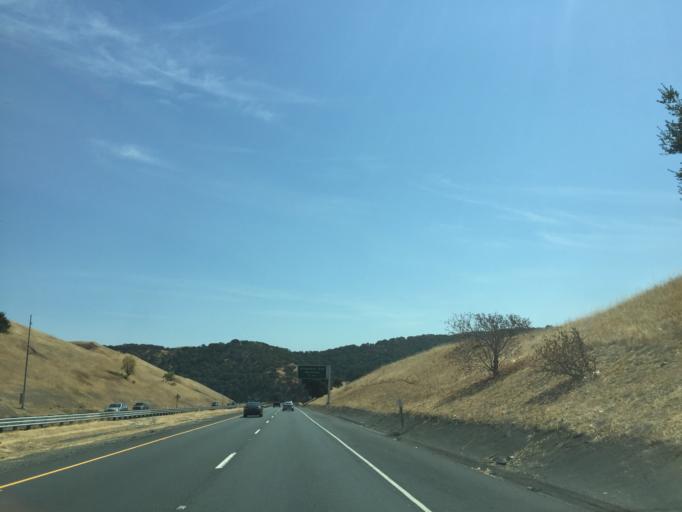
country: US
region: California
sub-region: Contra Costa County
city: Martinez
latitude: 37.9966
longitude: -122.1454
